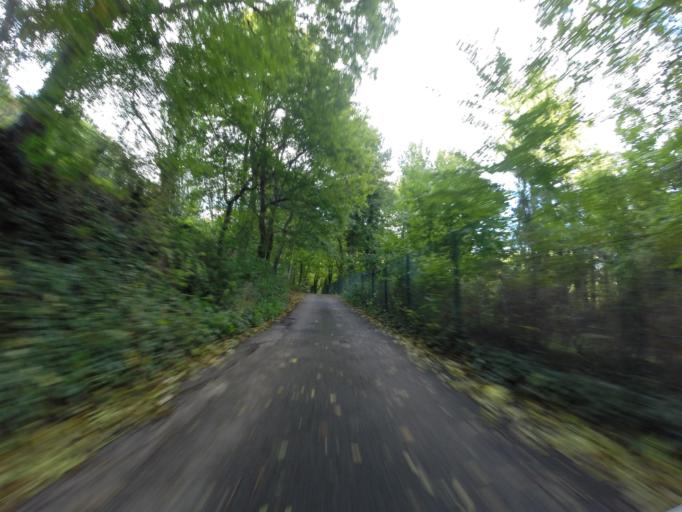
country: DE
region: Thuringia
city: Jena
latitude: 50.9444
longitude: 11.5866
